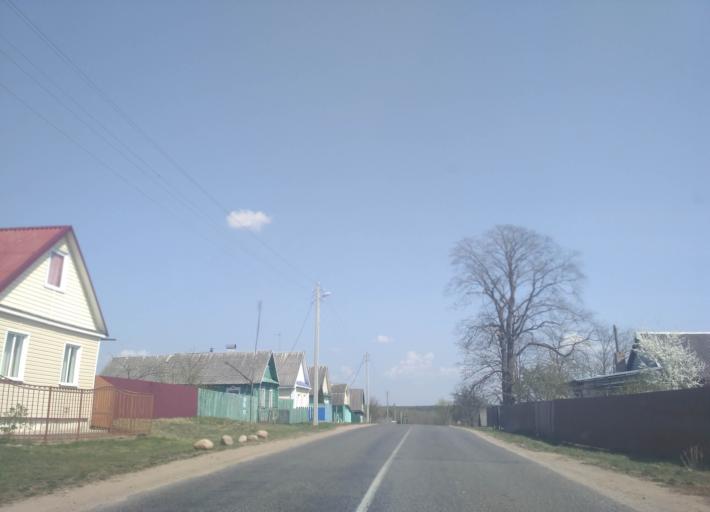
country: BY
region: Minsk
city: Loshnitsa
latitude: 54.4095
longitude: 28.6272
